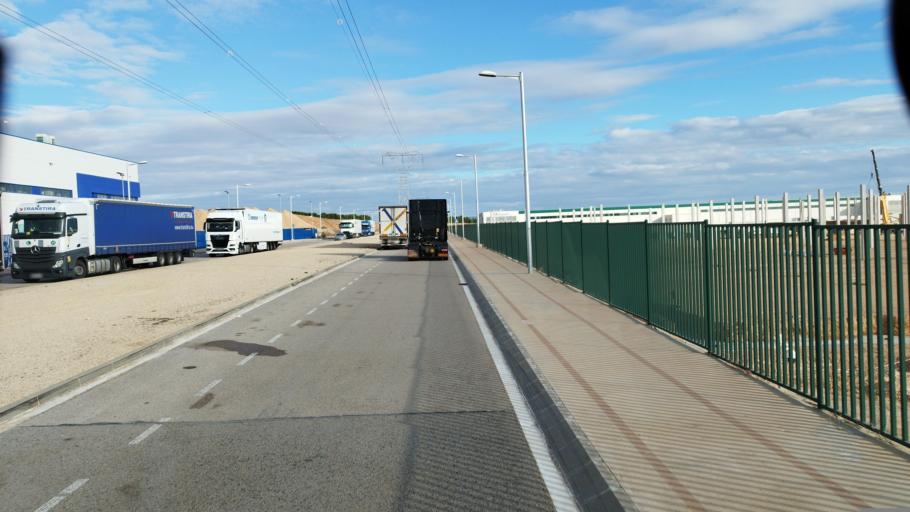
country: ES
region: Catalonia
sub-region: Provincia de Tarragona
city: la Bisbal del Penedes
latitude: 41.2757
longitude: 1.5079
